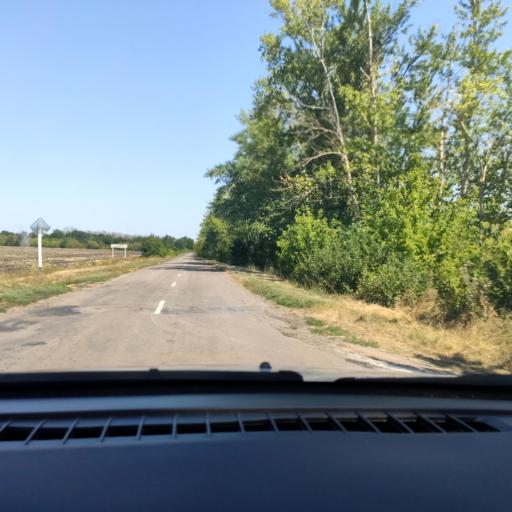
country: RU
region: Voronezj
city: Ostrogozhsk
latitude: 50.7090
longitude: 39.3354
